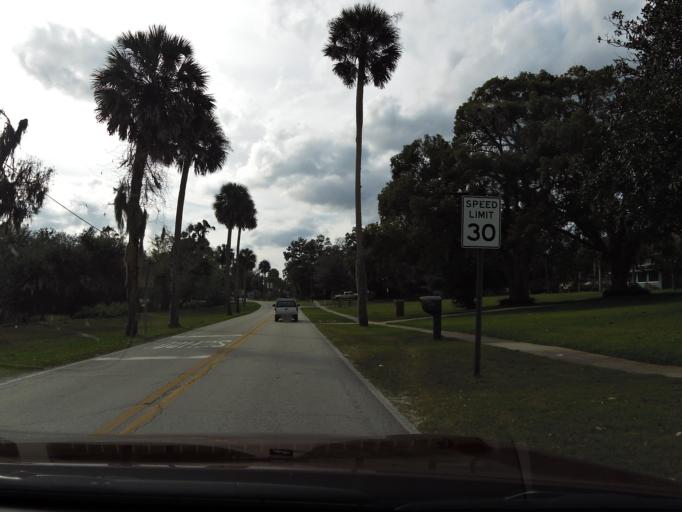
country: US
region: Florida
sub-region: Volusia County
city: Orange City
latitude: 28.9488
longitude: -81.2937
